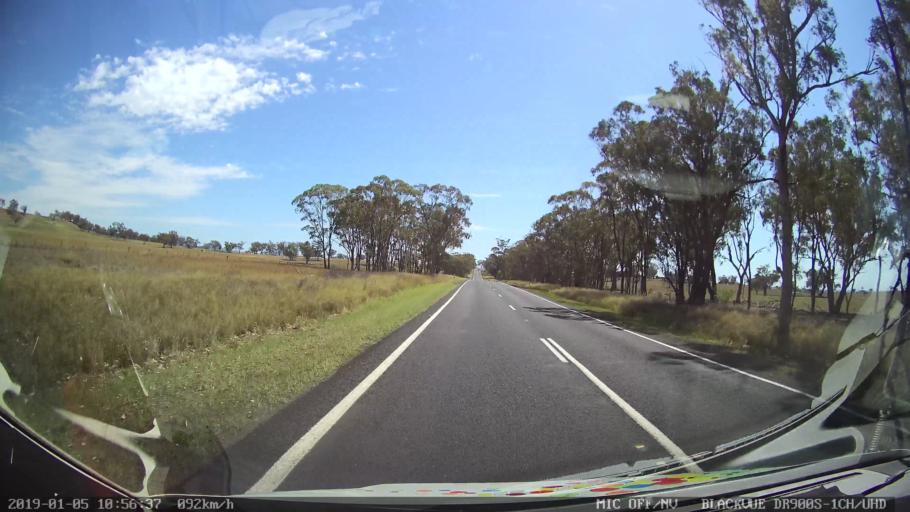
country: AU
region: New South Wales
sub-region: Warrumbungle Shire
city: Coonabarabran
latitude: -31.4396
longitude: 149.1600
